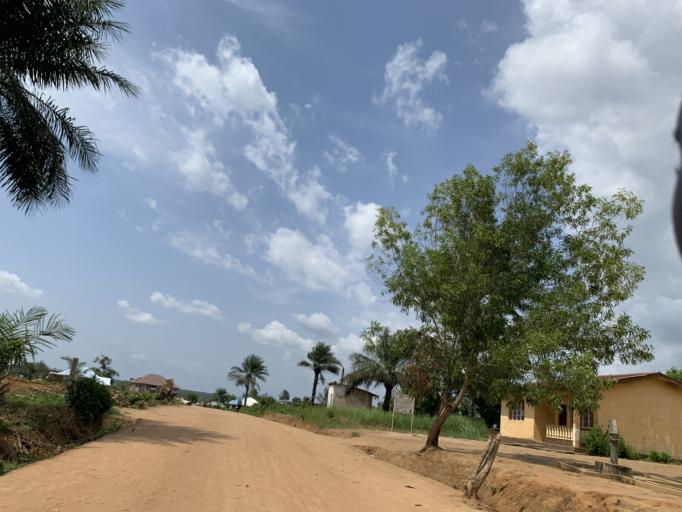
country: SL
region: Western Area
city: Waterloo
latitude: 8.3624
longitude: -13.0435
